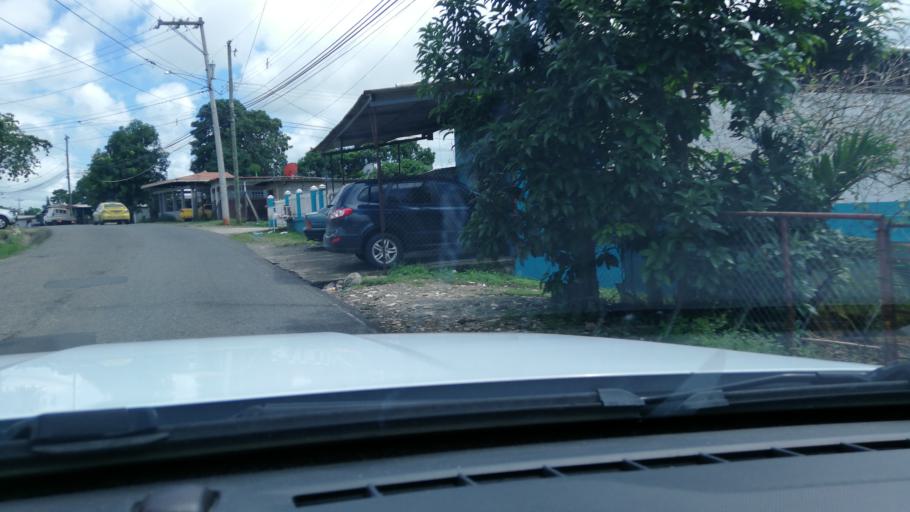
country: PA
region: Panama
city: Cabra Numero Uno
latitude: 9.1068
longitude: -79.3355
